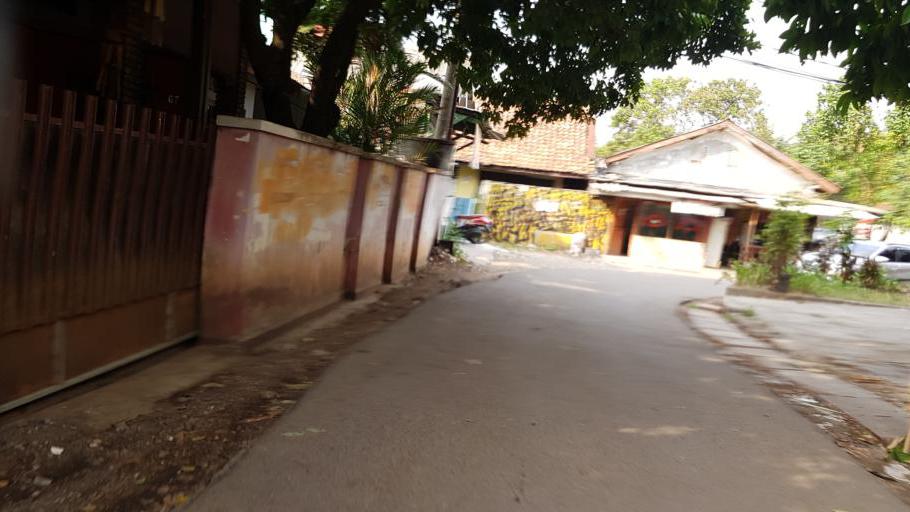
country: ID
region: West Java
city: Pamulang
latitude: -6.3285
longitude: 106.7993
